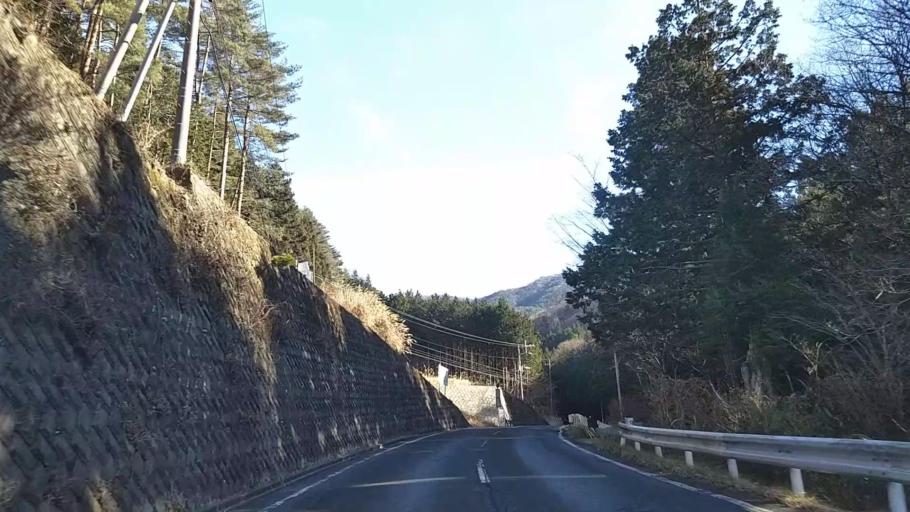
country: JP
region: Yamanashi
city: Otsuki
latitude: 35.5133
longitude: 138.9441
